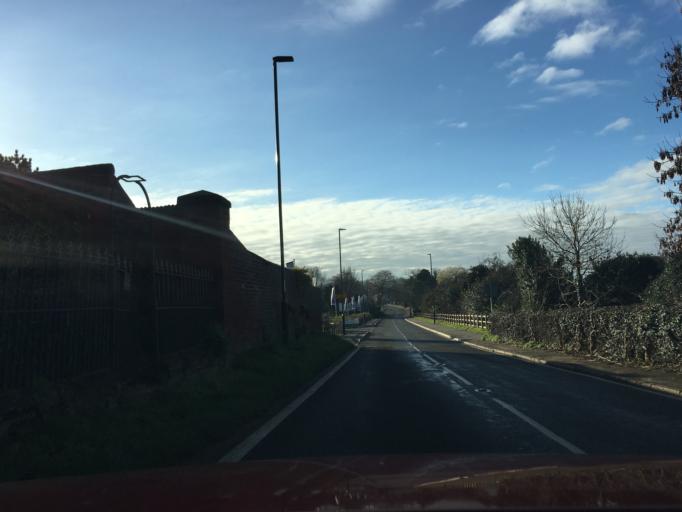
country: GB
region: England
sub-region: Staffordshire
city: Burton upon Trent
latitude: 52.8170
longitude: -1.6084
